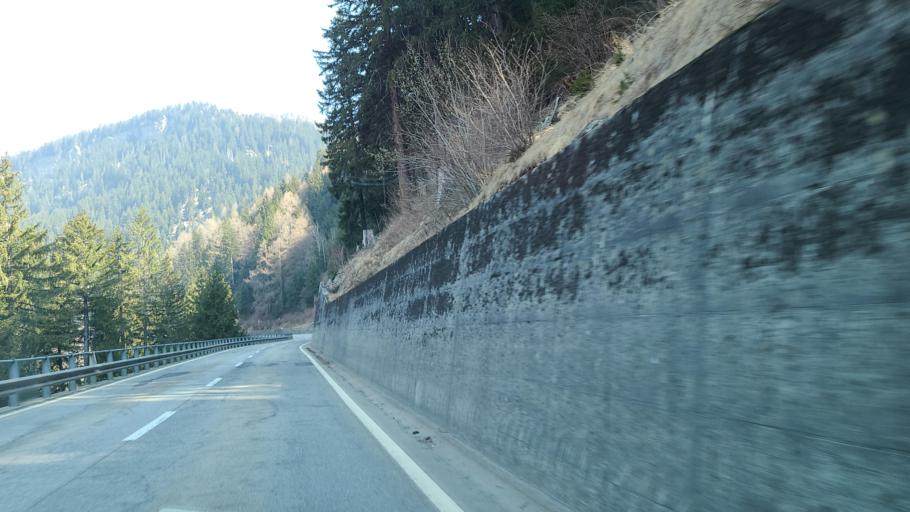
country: CH
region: Grisons
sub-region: Bernina District
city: Poschiavo
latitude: 46.3544
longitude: 10.0760
